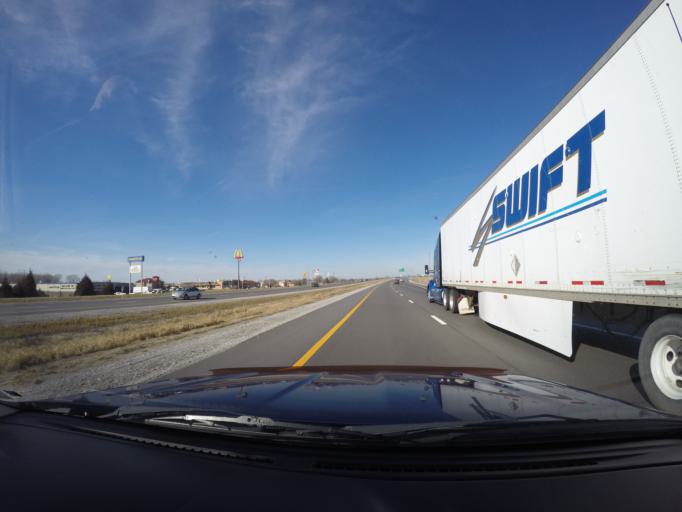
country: US
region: Kansas
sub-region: Sedgwick County
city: Park City
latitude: 37.7911
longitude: -97.3274
